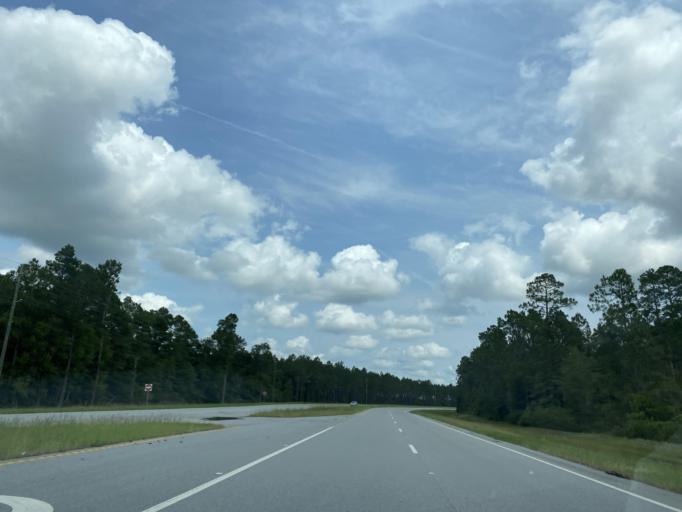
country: US
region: Georgia
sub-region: Ware County
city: Deenwood
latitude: 31.2713
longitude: -82.4377
